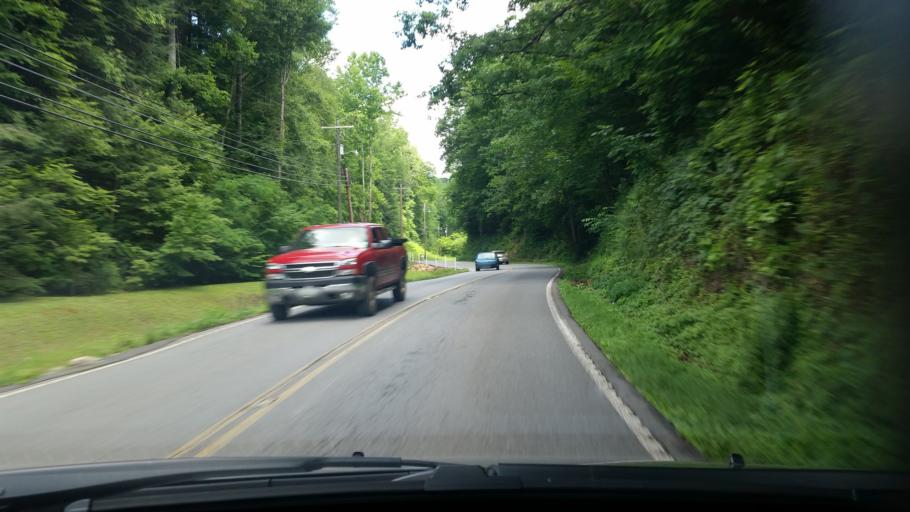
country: US
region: Tennessee
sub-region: Sevier County
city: Gatlinburg
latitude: 35.7312
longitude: -83.4678
